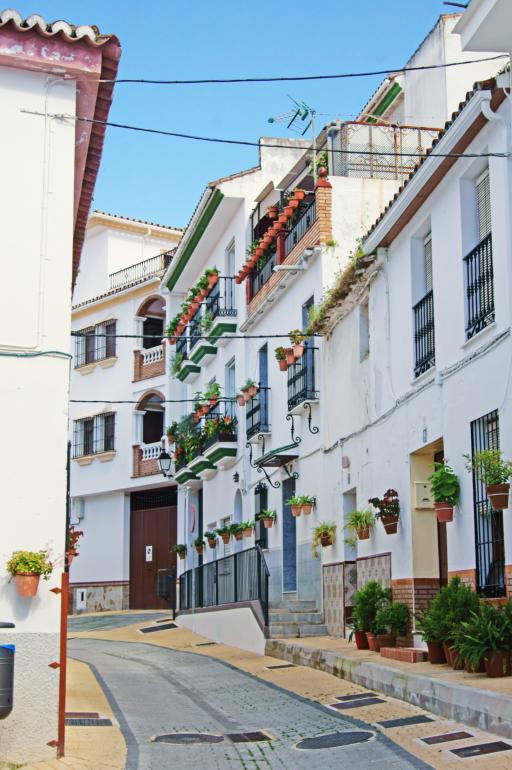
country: ES
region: Andalusia
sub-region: Provincia de Malaga
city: Monda
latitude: 36.6288
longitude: -4.8304
